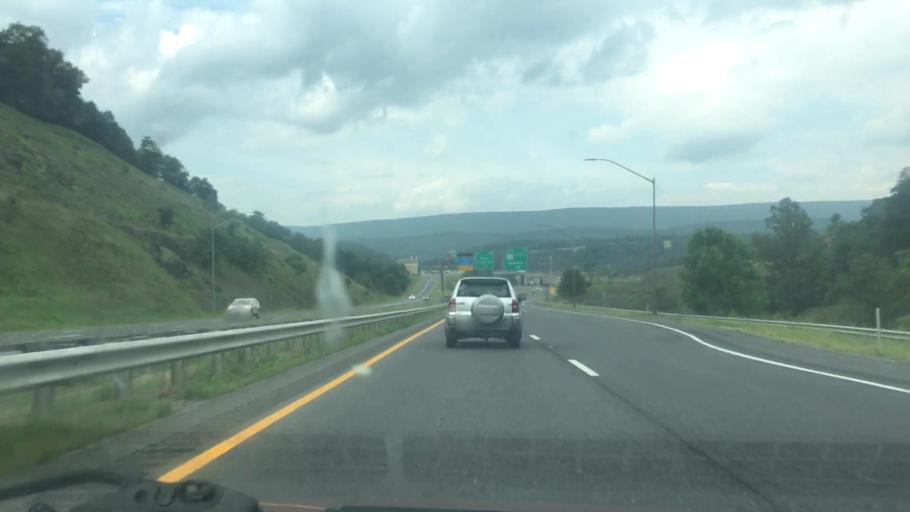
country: US
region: Maryland
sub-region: Allegany County
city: Cumberland
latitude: 39.6702
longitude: -78.7064
